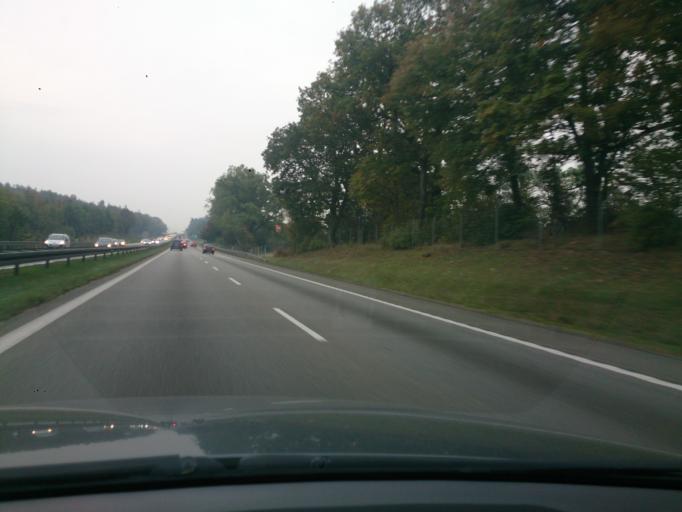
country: PL
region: Pomeranian Voivodeship
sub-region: Gdynia
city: Wielki Kack
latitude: 54.3900
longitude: 18.4945
